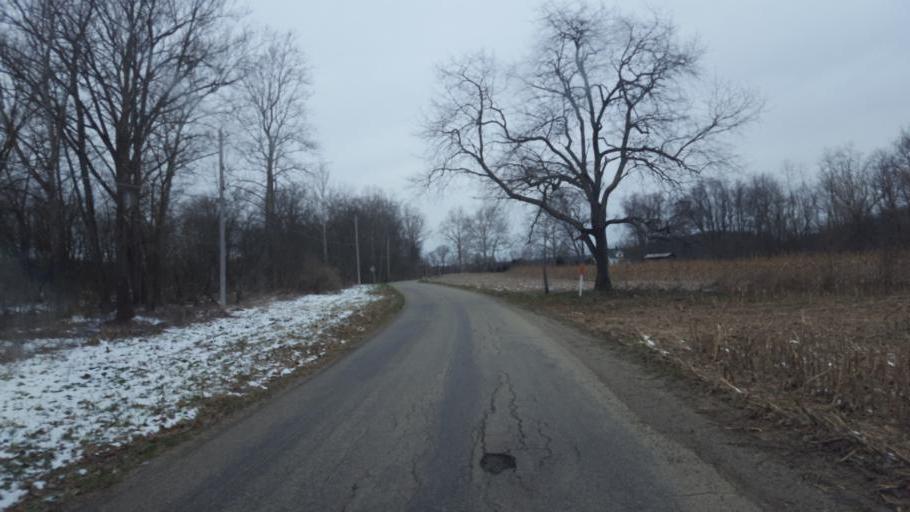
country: US
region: Ohio
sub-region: Sandusky County
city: Bellville
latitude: 40.5988
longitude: -82.4466
